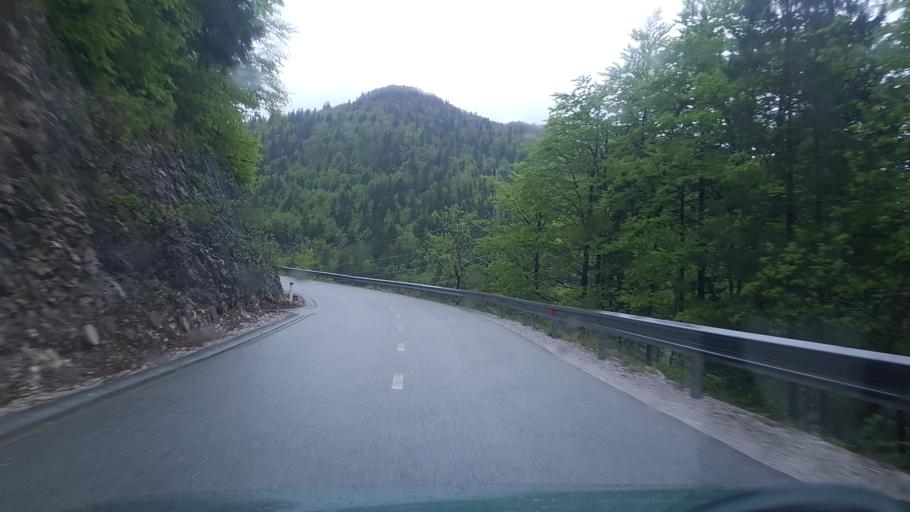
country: SI
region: Bohinj
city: Bohinjska Bistrica
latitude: 46.2521
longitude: 14.0045
